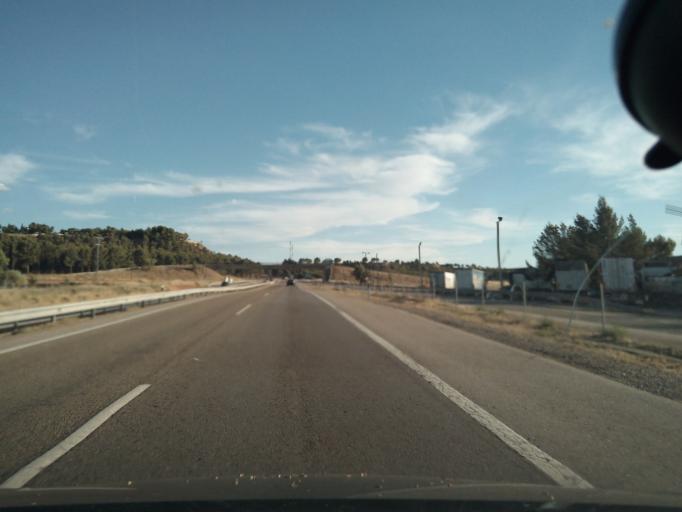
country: ES
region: Castille-La Mancha
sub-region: Province of Toledo
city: Dosbarrios
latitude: 39.7939
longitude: -3.4814
